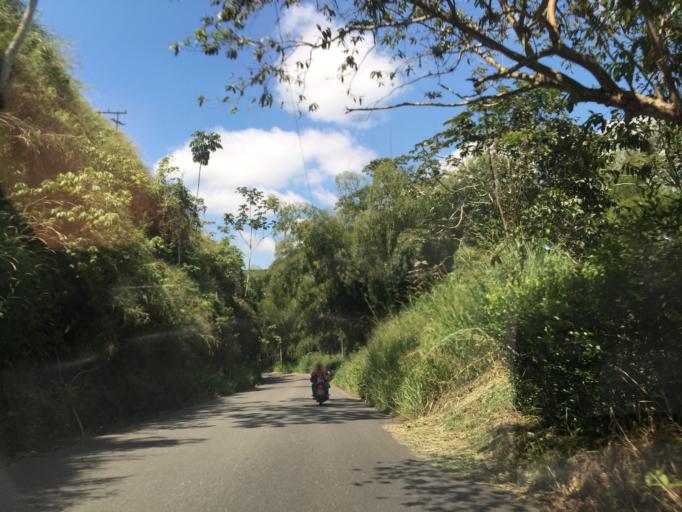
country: CO
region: Valle del Cauca
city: Alcala
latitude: 4.6981
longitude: -75.7871
